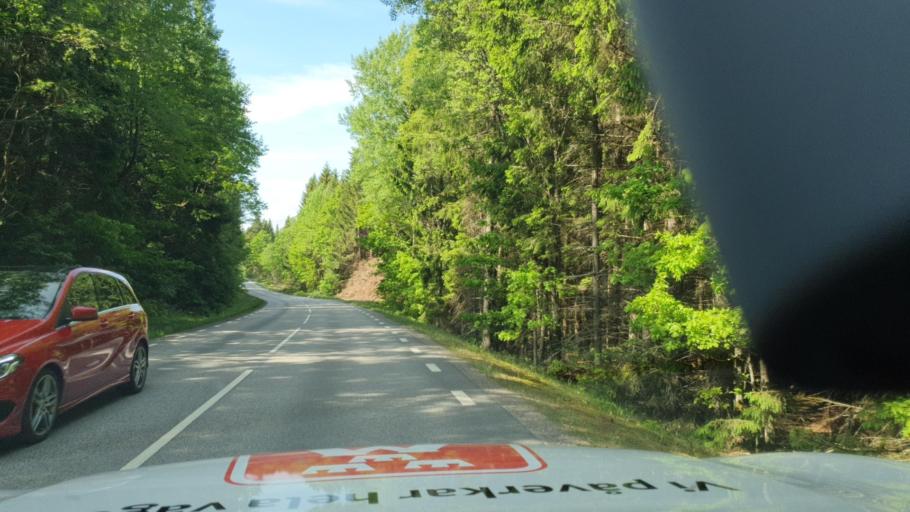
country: SE
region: Vaestra Goetaland
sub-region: Herrljunga Kommun
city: Herrljunga
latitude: 58.0176
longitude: 13.1374
